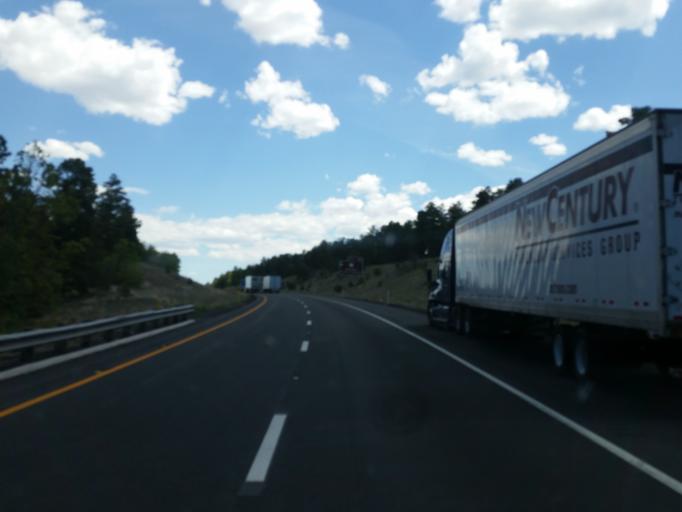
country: US
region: Arizona
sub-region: Coconino County
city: Williams
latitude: 35.2248
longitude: -112.2378
